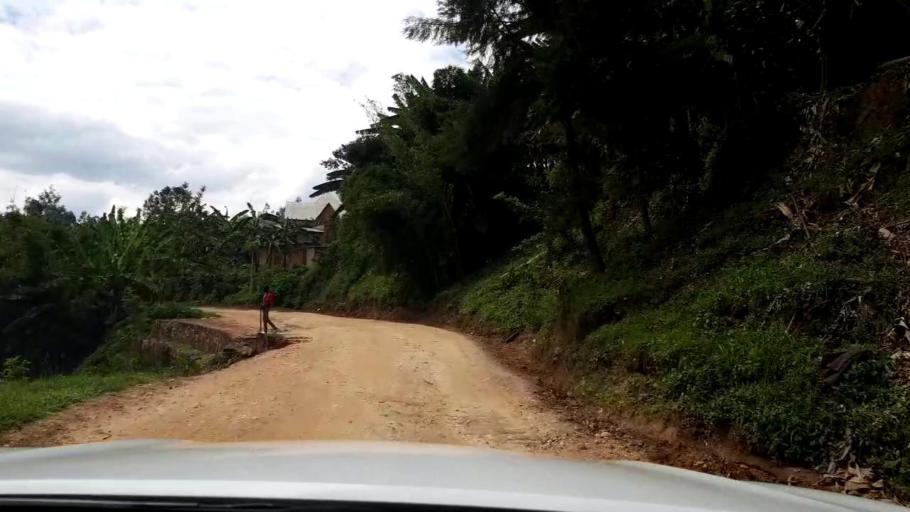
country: RW
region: Southern Province
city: Gitarama
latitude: -1.9249
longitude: 29.6533
